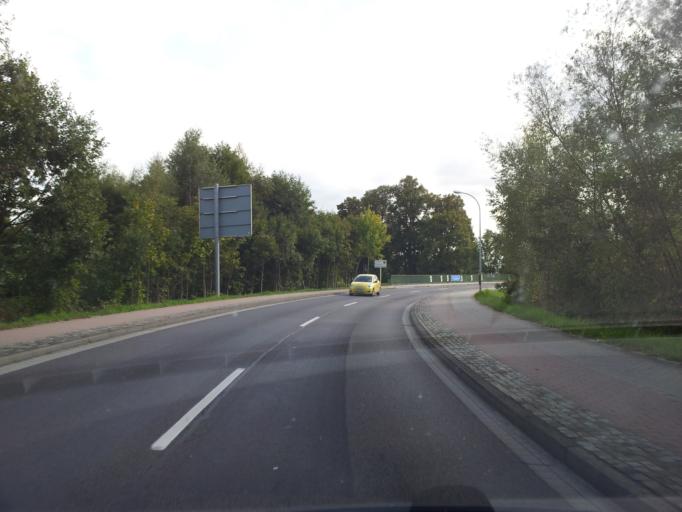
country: DE
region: Brandenburg
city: Ruhland
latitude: 51.4638
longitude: 13.8691
